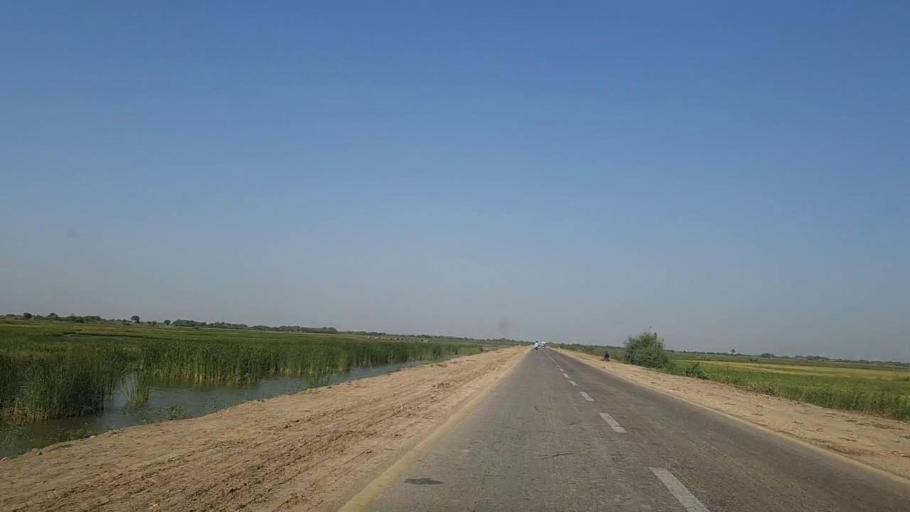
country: PK
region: Sindh
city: Jati
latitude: 24.4179
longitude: 68.3043
